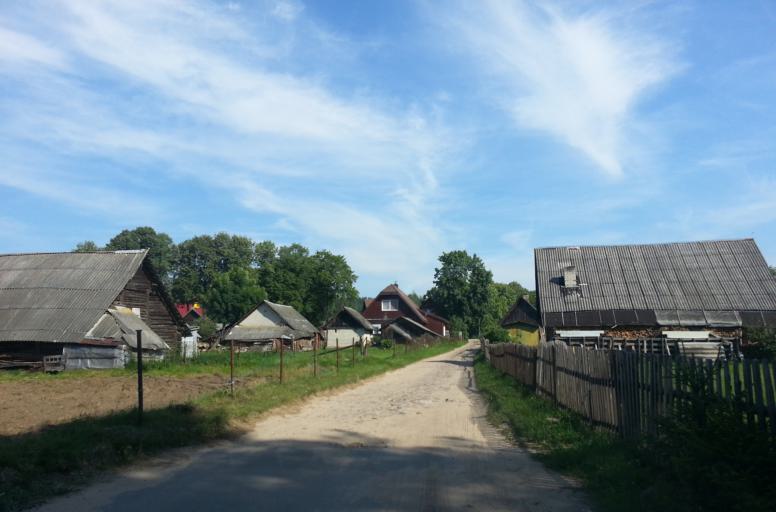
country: LT
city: Grigiskes
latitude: 54.7298
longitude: 25.0448
